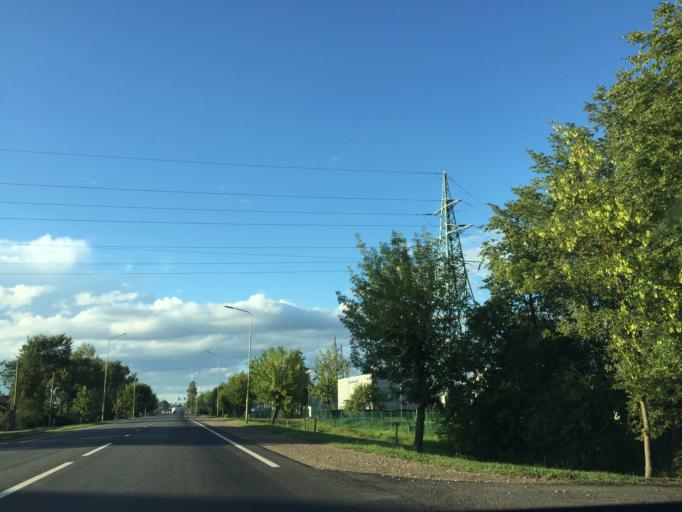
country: LV
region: Jelgava
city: Jelgava
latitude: 56.6262
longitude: 23.7252
